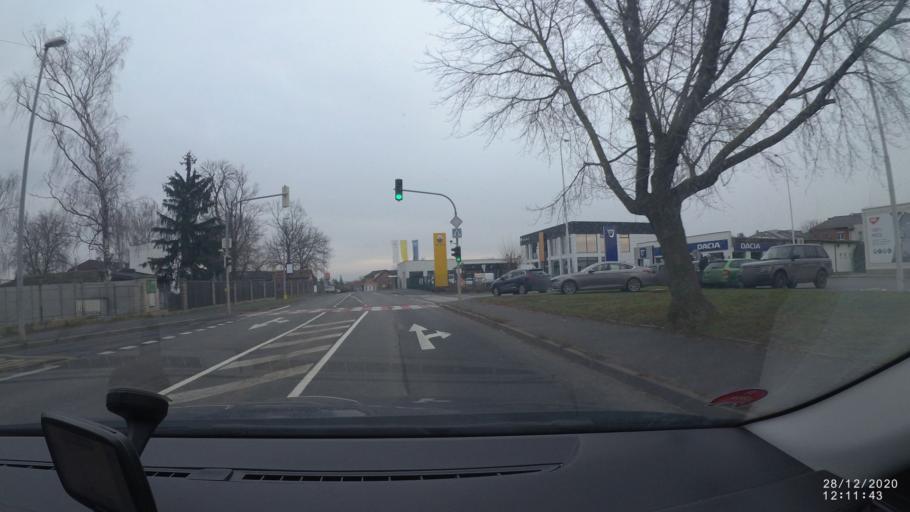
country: CZ
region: Central Bohemia
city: Brandys nad Labem-Stara Boleslav
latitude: 50.1742
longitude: 14.6484
